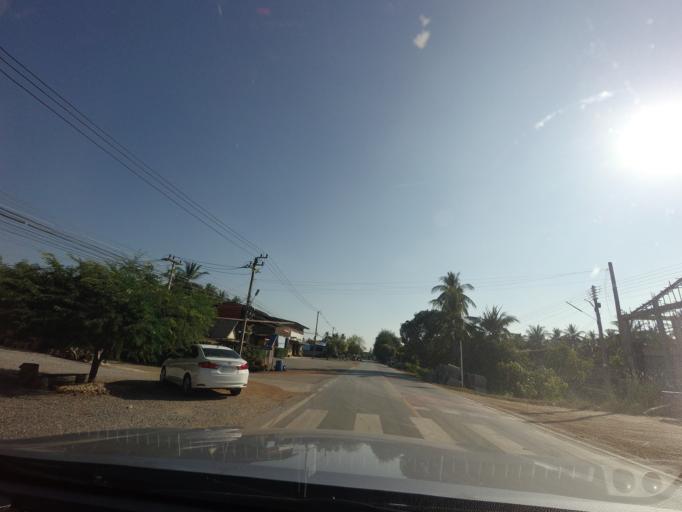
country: TH
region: Sukhothai
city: Sawankhalok
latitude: 17.4160
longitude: 99.7988
